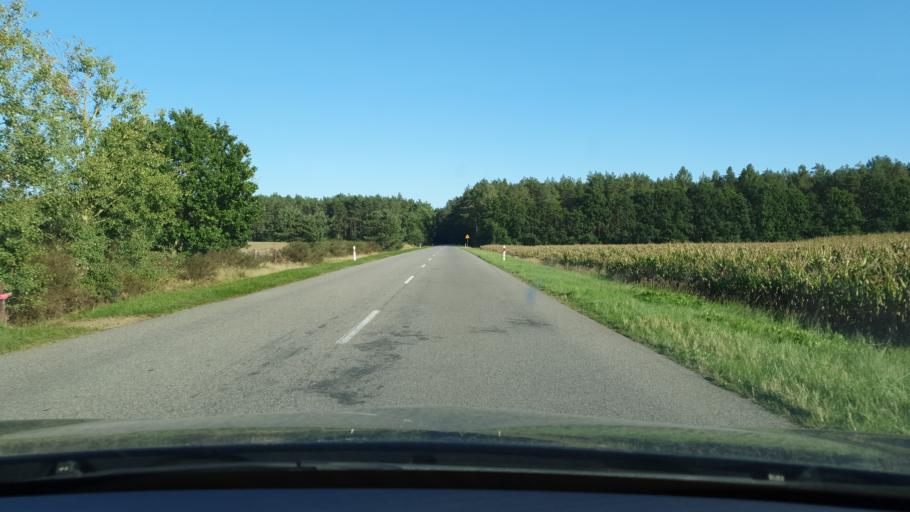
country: PL
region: West Pomeranian Voivodeship
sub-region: Powiat kamienski
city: Golczewo
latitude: 53.8158
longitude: 15.0534
